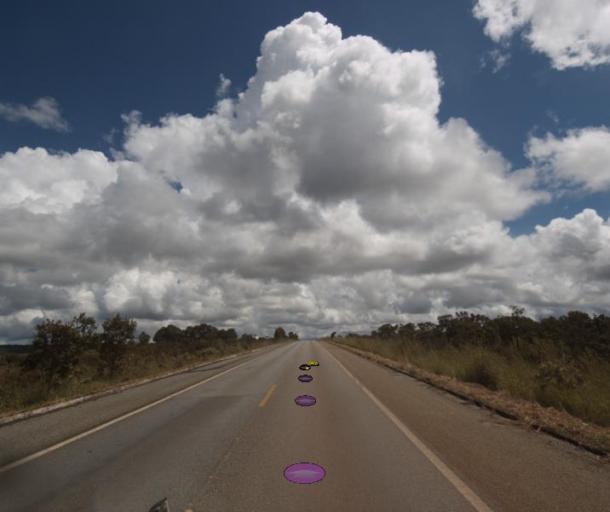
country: BR
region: Goias
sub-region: Pirenopolis
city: Pirenopolis
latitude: -15.7638
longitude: -48.7015
